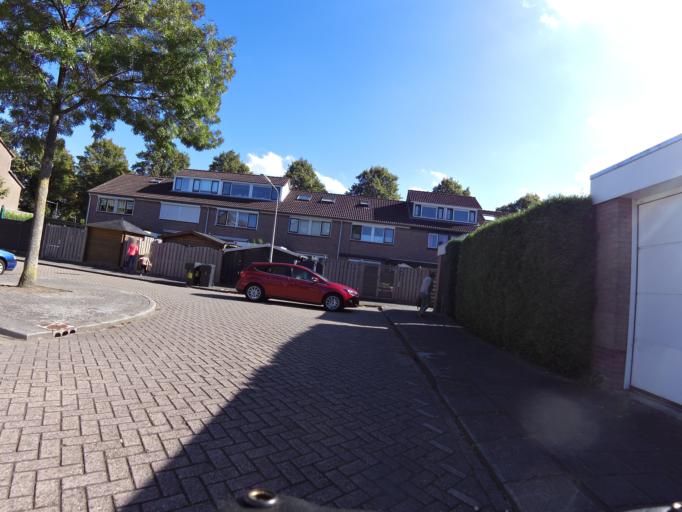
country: NL
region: South Holland
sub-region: Gemeente Zwijndrecht
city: Zwijndrecht
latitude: 51.7836
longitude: 4.6125
